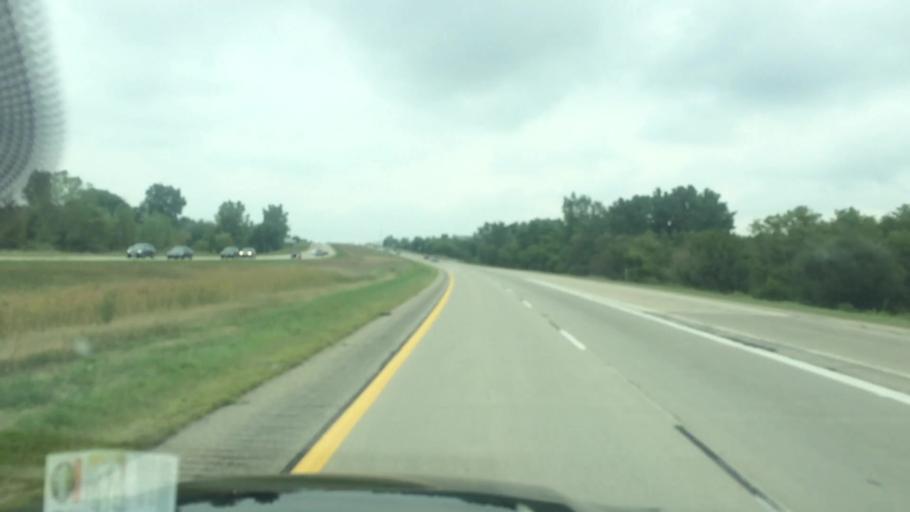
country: US
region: Michigan
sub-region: Eaton County
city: Dimondale
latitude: 42.6620
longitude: -84.6824
